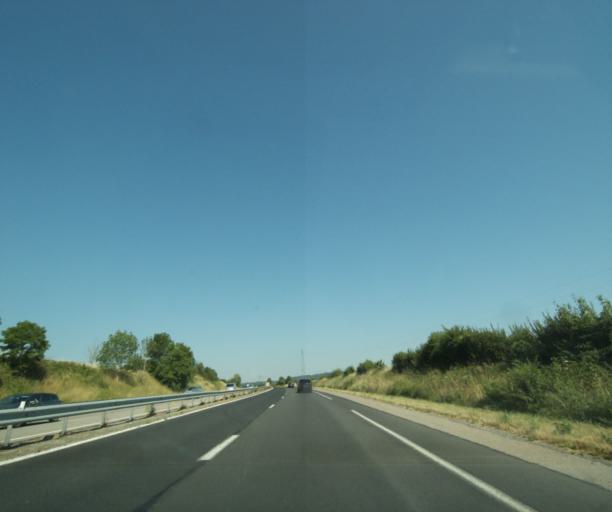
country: FR
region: Lorraine
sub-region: Departement de Meurthe-et-Moselle
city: Ecrouves
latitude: 48.6646
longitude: 5.8291
